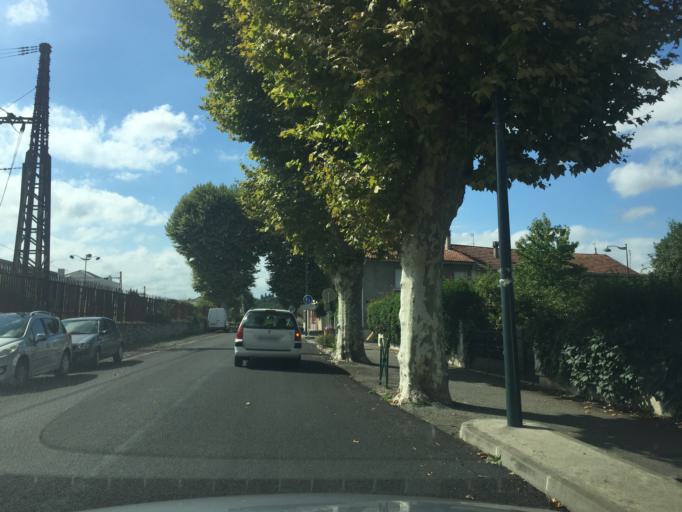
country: FR
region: Midi-Pyrenees
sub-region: Departement de la Haute-Garonne
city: Gourdan-Polignan
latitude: 43.0781
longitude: 0.5753
